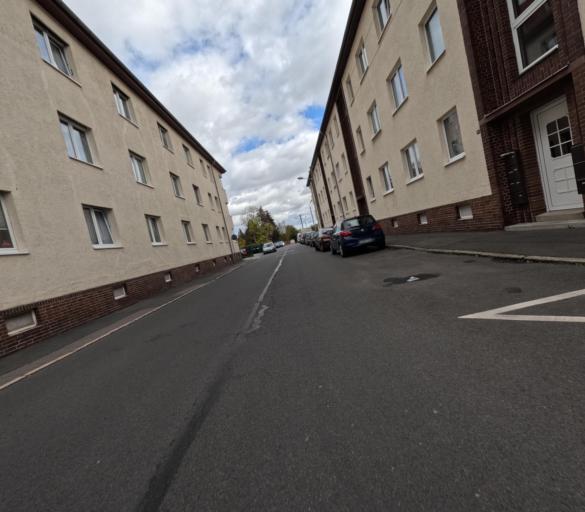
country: DE
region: Saxony
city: Grimma
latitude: 51.2333
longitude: 12.7164
